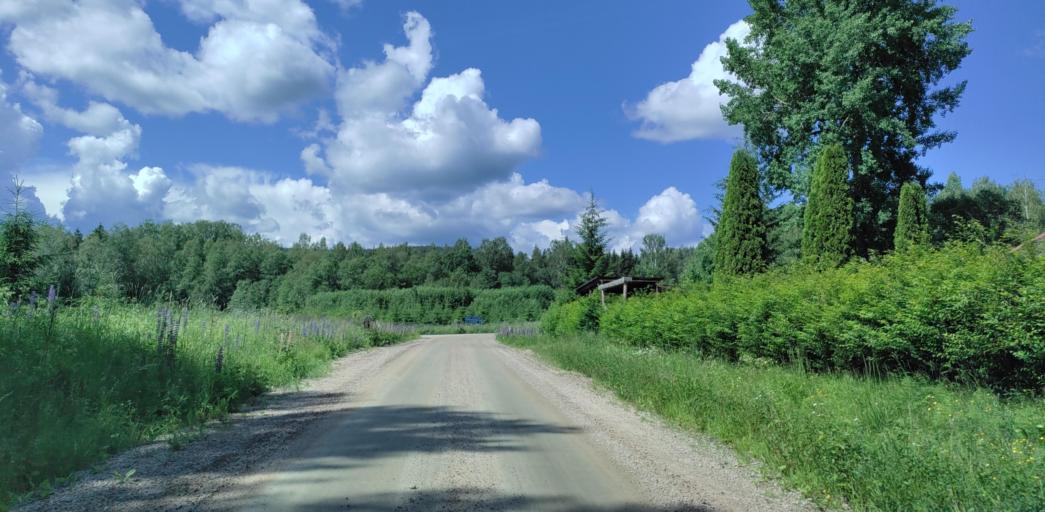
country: SE
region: Vaermland
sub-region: Hagfors Kommun
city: Ekshaerad
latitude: 60.0138
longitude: 13.4727
